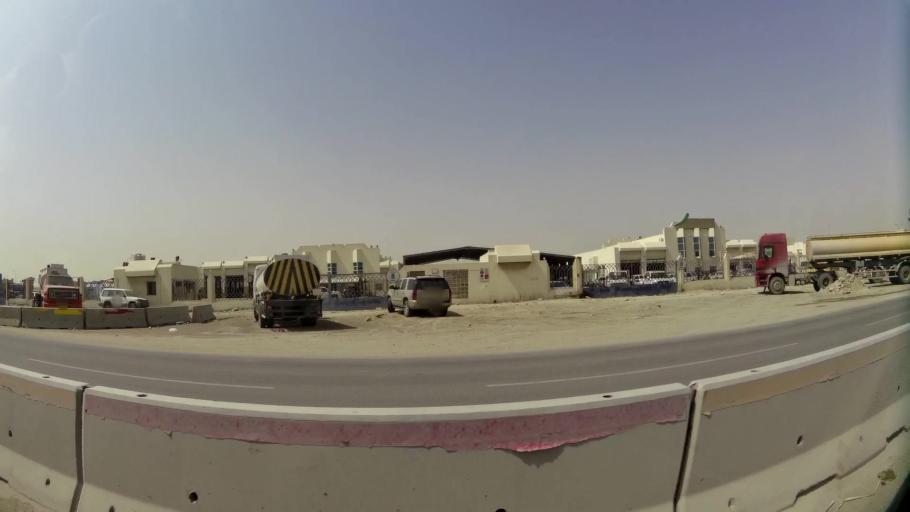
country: QA
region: Baladiyat ar Rayyan
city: Ar Rayyan
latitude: 25.1918
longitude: 51.4341
